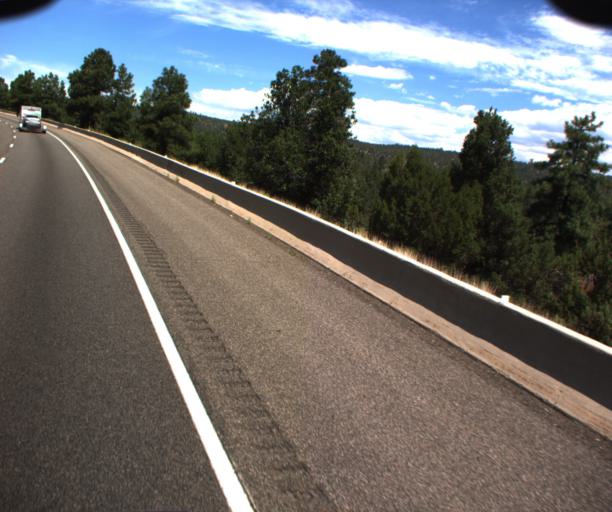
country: US
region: Arizona
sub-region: Yavapai County
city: Village of Oak Creek (Big Park)
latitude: 34.7982
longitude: -111.5905
